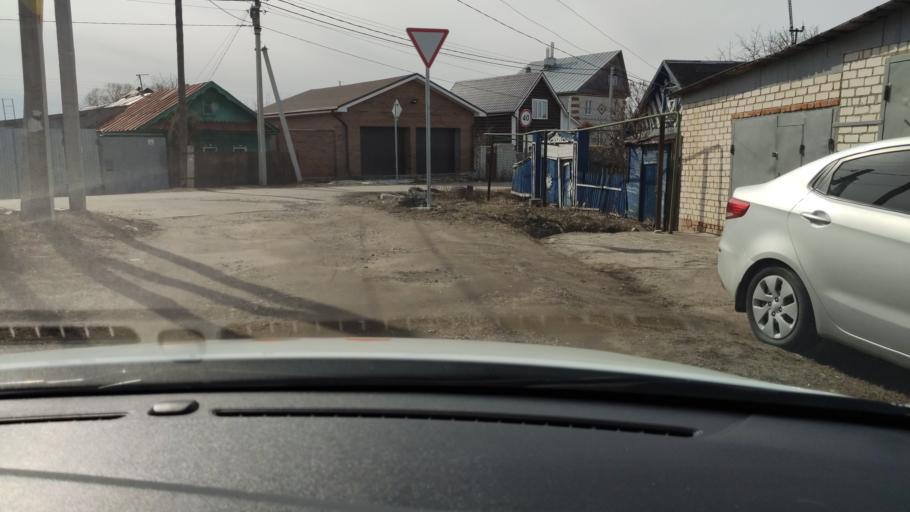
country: RU
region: Tatarstan
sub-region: Gorod Kazan'
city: Kazan
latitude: 55.7257
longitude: 49.1409
